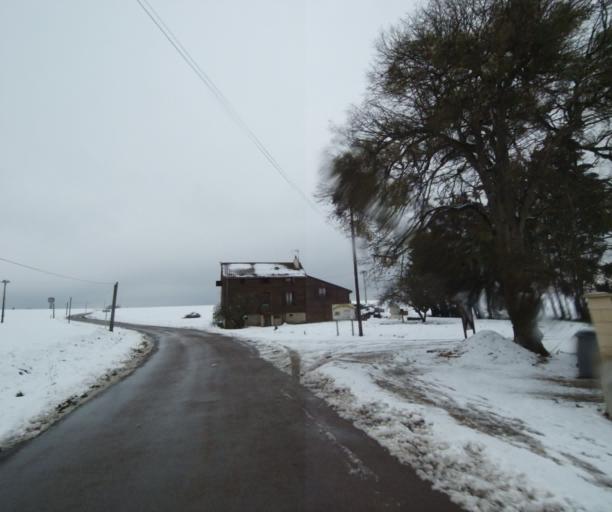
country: FR
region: Champagne-Ardenne
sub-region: Departement de la Haute-Marne
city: Laneuville-a-Remy
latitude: 48.5094
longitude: 4.8484
